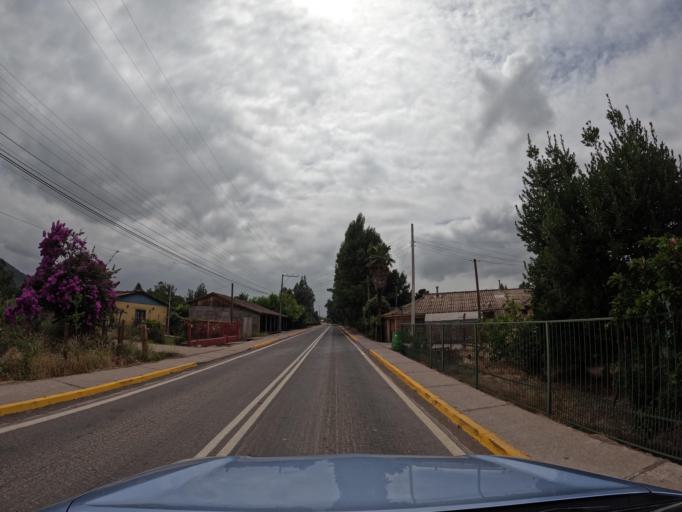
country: CL
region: Maule
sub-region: Provincia de Curico
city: Teno
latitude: -34.7777
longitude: -71.1732
